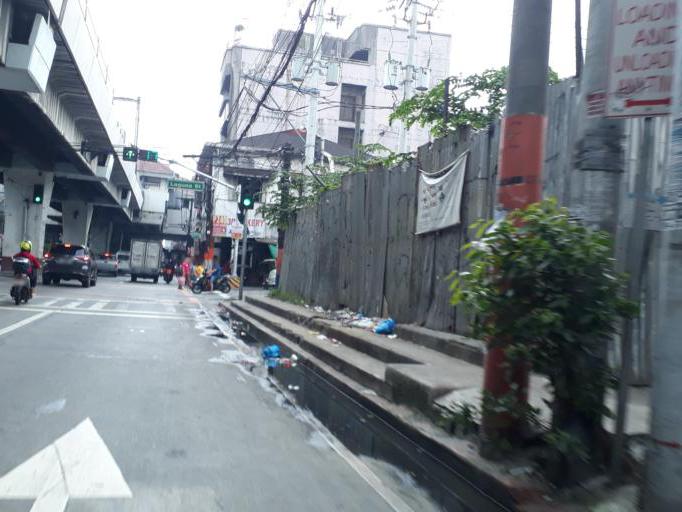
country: PH
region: Metro Manila
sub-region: City of Manila
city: Manila
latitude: 14.6215
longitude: 120.9830
